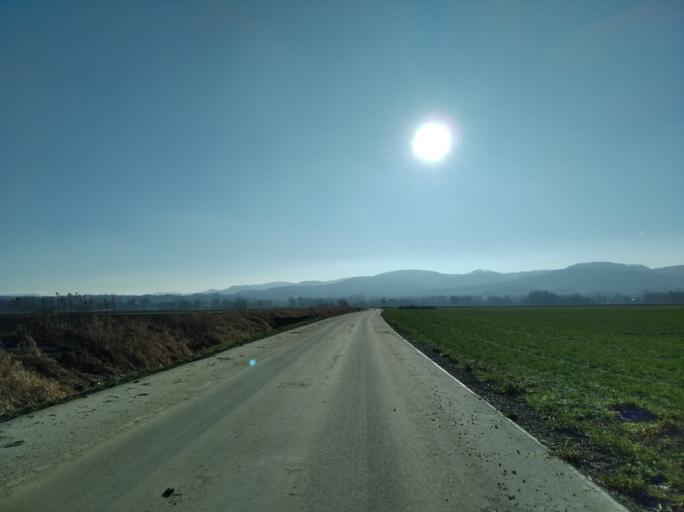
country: PL
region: Subcarpathian Voivodeship
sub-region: Powiat strzyzowski
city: Wisniowa
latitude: 49.8689
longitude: 21.6954
